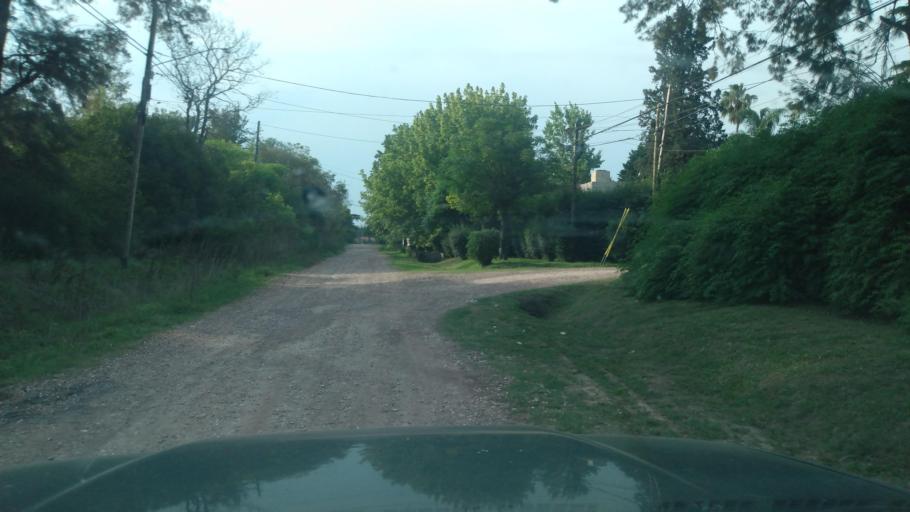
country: AR
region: Buenos Aires
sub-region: Partido de Lujan
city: Lujan
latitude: -34.5532
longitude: -59.1299
